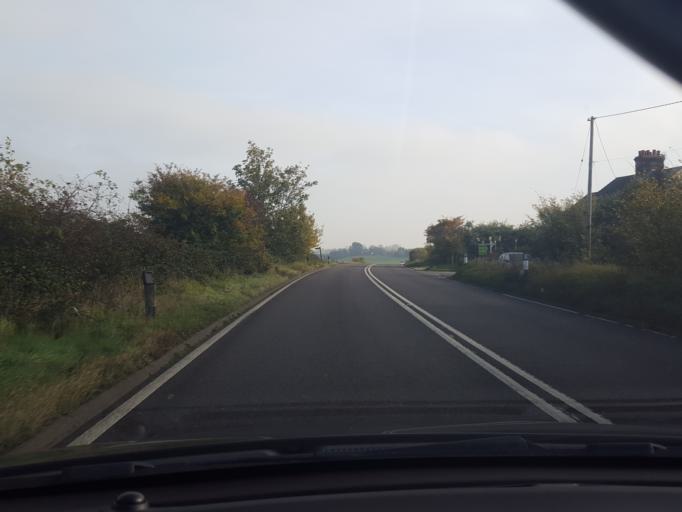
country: GB
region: England
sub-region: Suffolk
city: Shotley Gate
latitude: 51.9245
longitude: 1.1863
